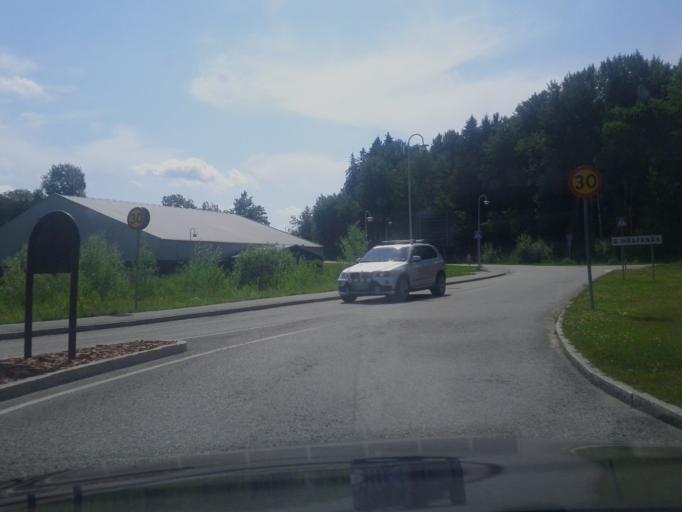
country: SE
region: Stockholm
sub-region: Taby Kommun
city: Taby
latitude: 59.4451
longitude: 18.1223
